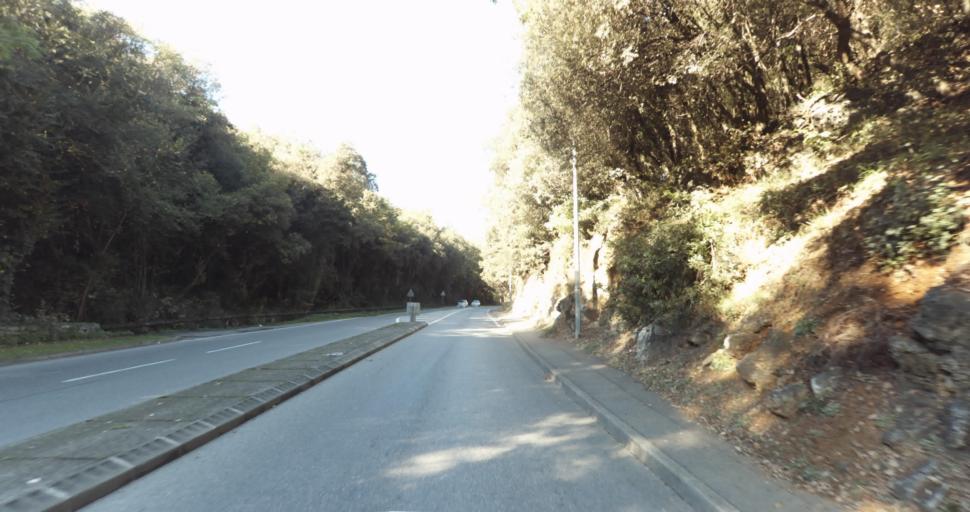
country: FR
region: Provence-Alpes-Cote d'Azur
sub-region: Departement des Alpes-Maritimes
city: Vence
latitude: 43.7156
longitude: 7.1159
